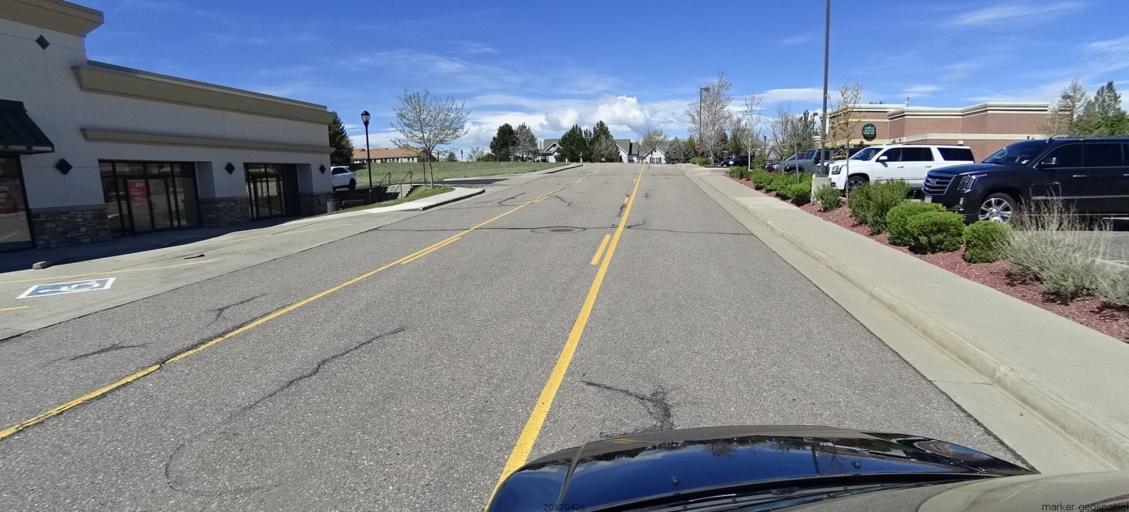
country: US
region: Colorado
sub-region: Adams County
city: Lone Tree
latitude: 39.5512
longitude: -104.8843
